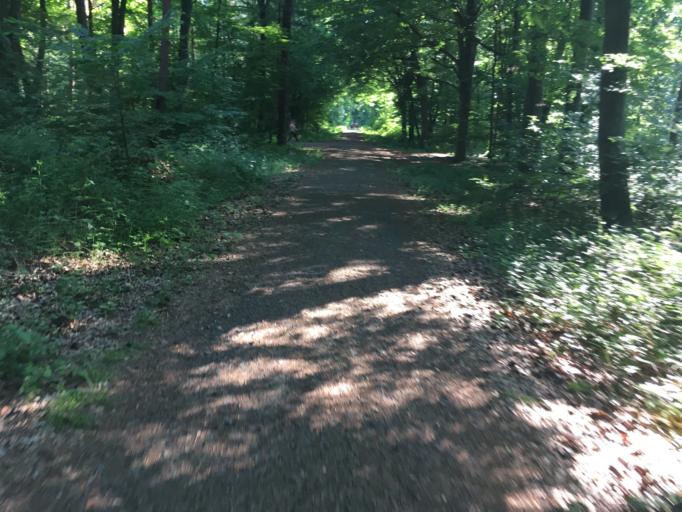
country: DE
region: Hesse
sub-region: Regierungsbezirk Darmstadt
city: Neu Isenburg
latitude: 50.0444
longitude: 8.6732
